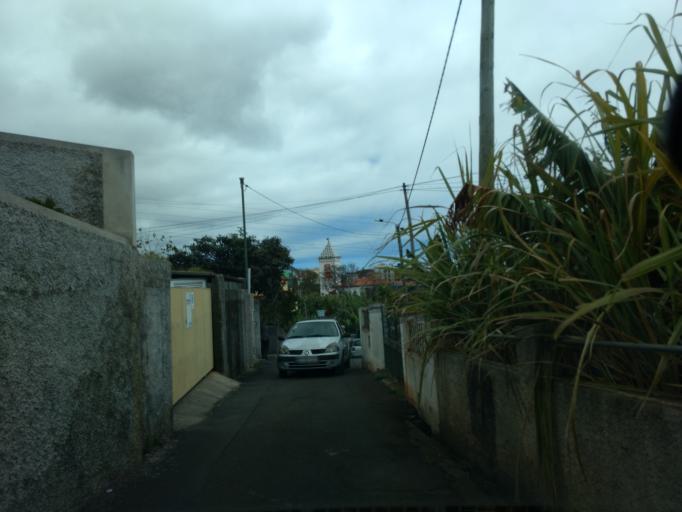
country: PT
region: Madeira
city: Camara de Lobos
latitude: 32.6610
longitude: -16.9520
